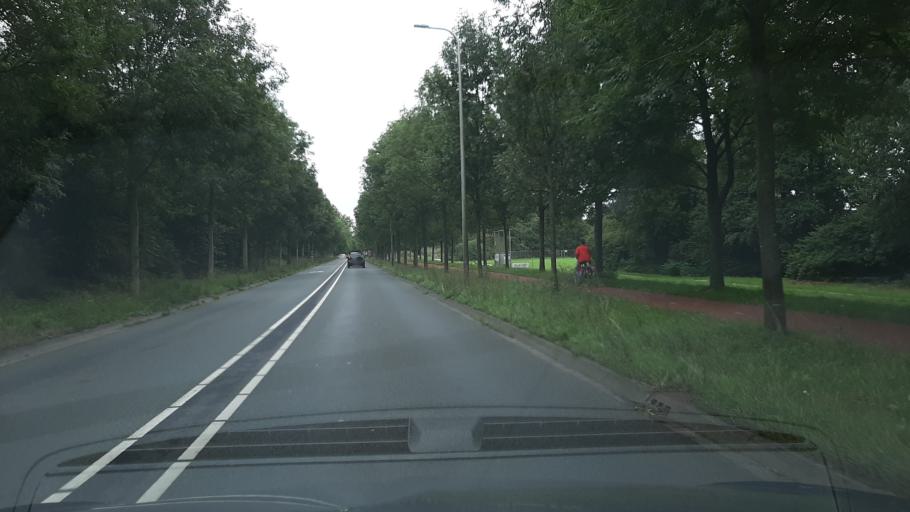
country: NL
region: Overijssel
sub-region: Gemeente Zwolle
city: Zwolle
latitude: 52.5339
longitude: 6.0785
